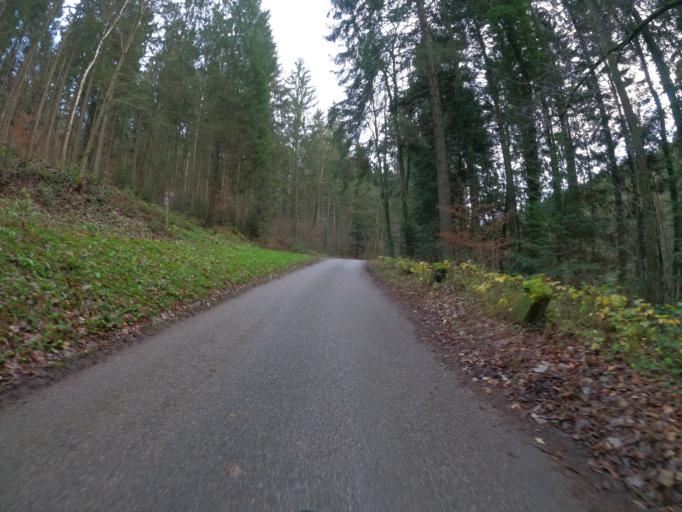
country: DE
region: Baden-Wuerttemberg
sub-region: Regierungsbezirk Stuttgart
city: Lorch
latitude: 48.7874
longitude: 9.7235
